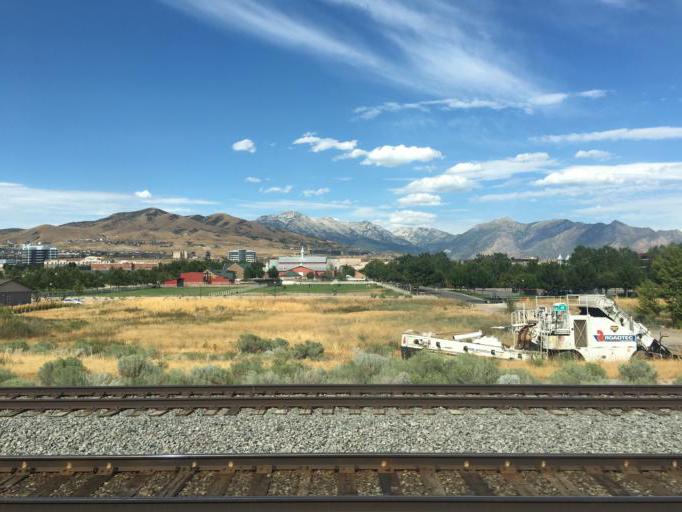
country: US
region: Utah
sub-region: Utah County
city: Lehi
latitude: 40.4212
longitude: -111.8918
